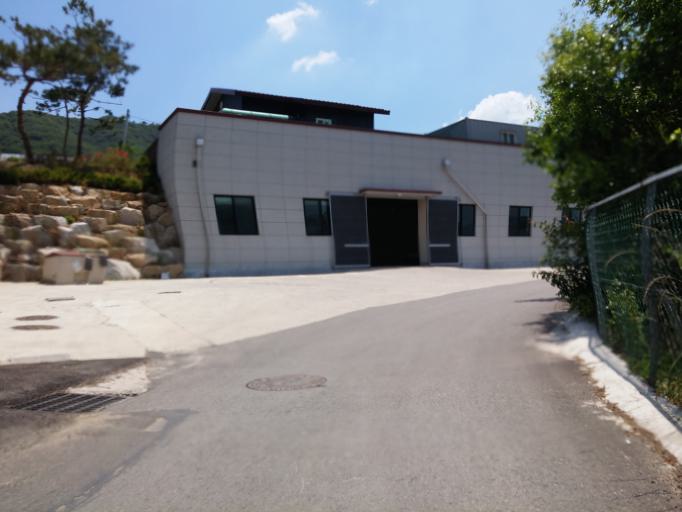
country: KR
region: Chungcheongbuk-do
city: Cheongju-si
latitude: 36.5548
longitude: 127.4346
